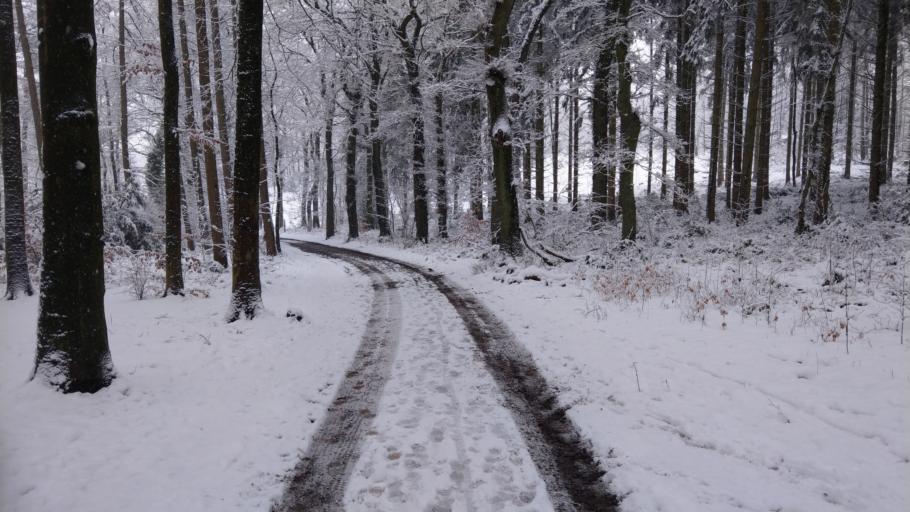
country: BE
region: Wallonia
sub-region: Province de Liege
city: La Calamine
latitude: 50.7182
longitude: 6.0505
